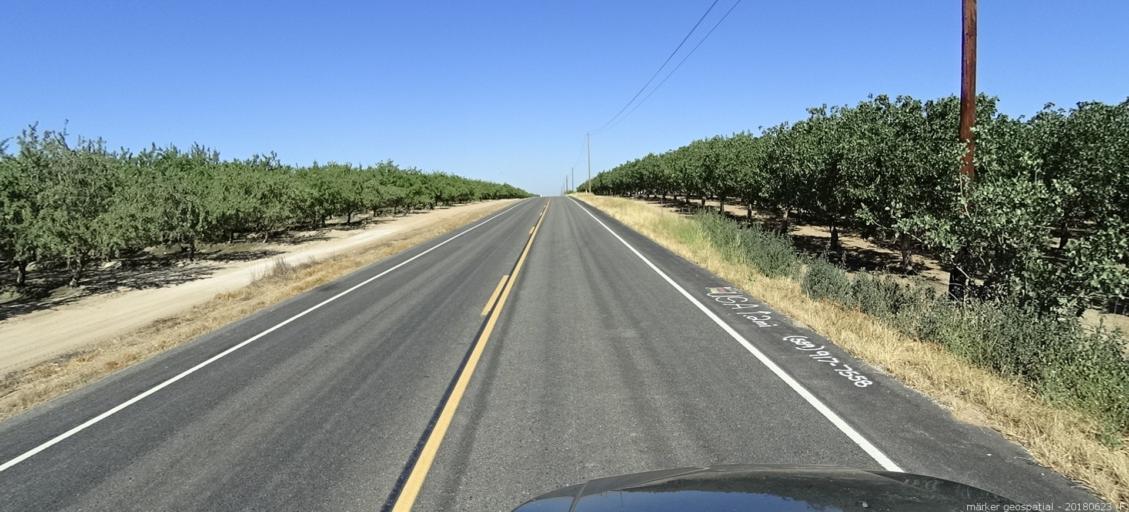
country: US
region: California
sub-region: Madera County
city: Parksdale
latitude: 36.9666
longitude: -119.9527
